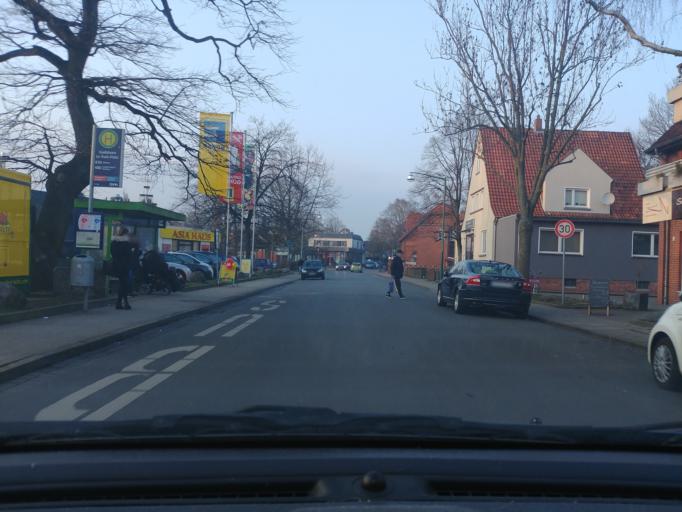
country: DE
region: Lower Saxony
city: Langenhagen
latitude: 52.4376
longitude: 9.7058
